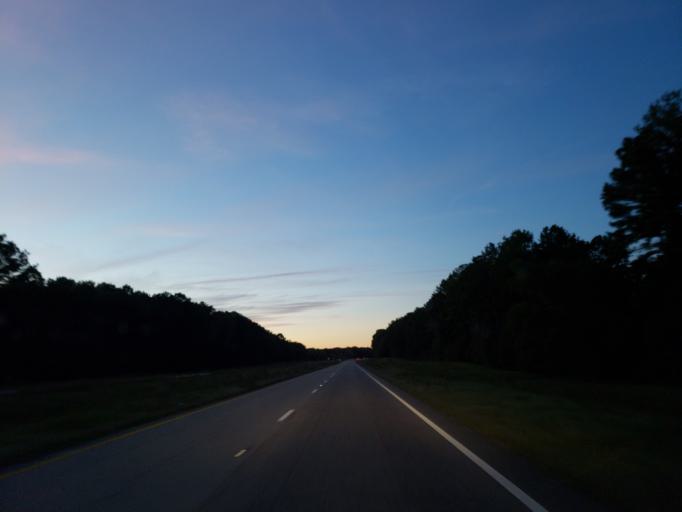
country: US
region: Mississippi
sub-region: Wayne County
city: Waynesboro
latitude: 31.8441
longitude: -88.7106
